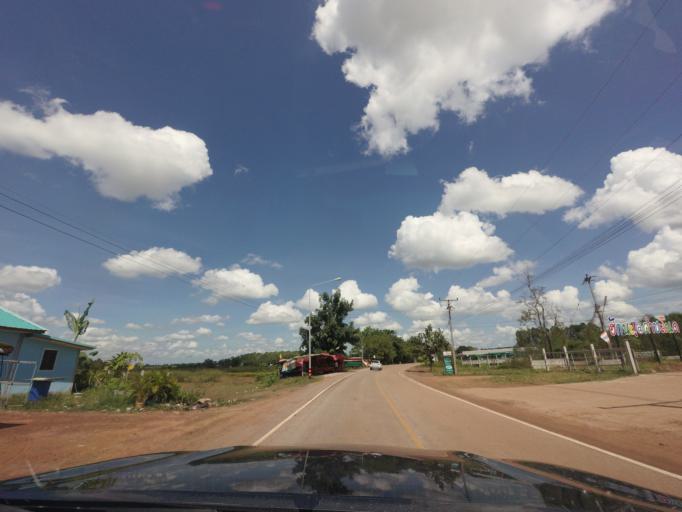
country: TH
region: Changwat Udon Thani
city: Ban Dung
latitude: 17.7410
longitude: 103.3541
